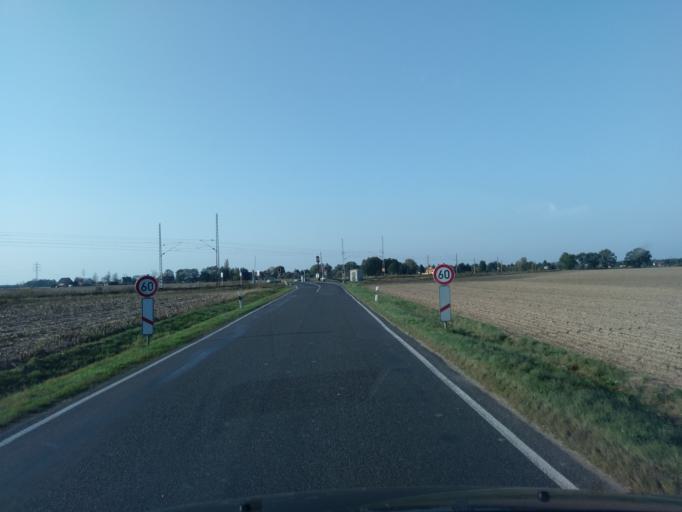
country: DE
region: Brandenburg
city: Falkenberg
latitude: 51.5625
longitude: 13.2571
